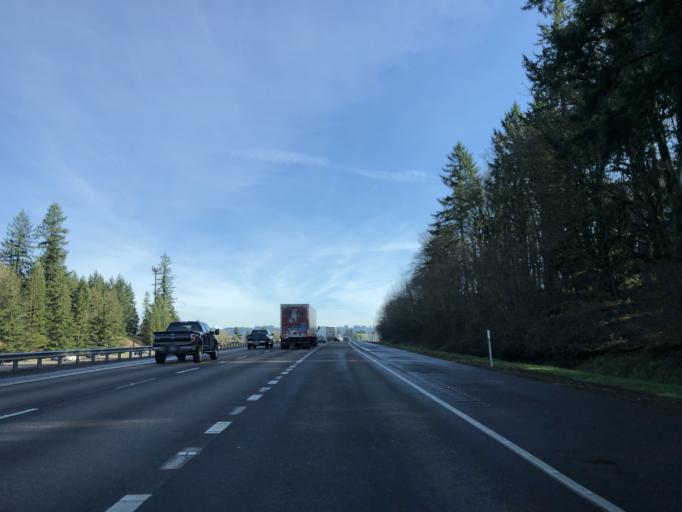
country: US
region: Oregon
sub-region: Clackamas County
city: Stafford
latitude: 45.3725
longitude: -122.7178
